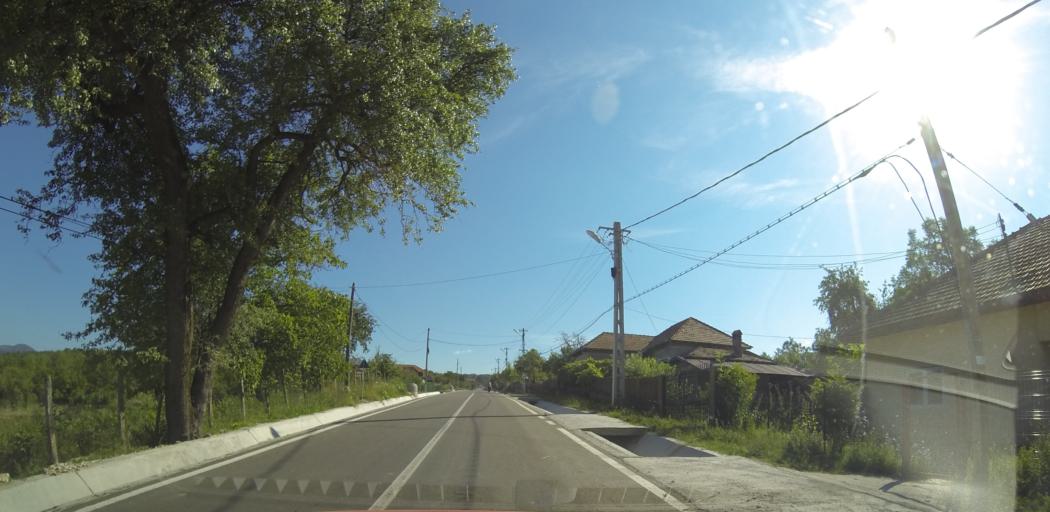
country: RO
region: Valcea
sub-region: Comuna Vaideeni
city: Vaideeni
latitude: 45.1636
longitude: 23.8963
